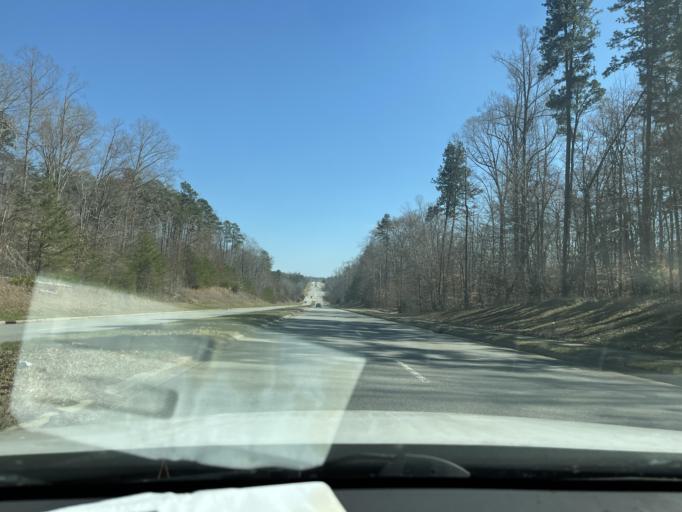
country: US
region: North Carolina
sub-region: Guilford County
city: Jamestown
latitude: 36.0105
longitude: -79.9257
